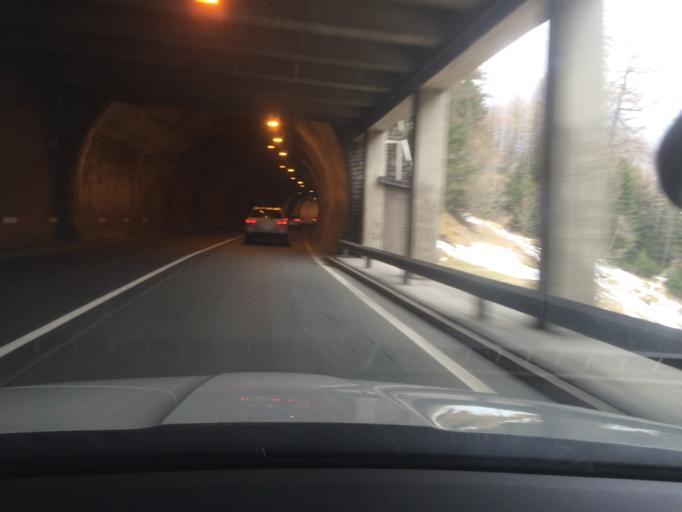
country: AT
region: Tyrol
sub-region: Politischer Bezirk Lienz
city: Matrei in Osttirol
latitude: 47.0607
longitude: 12.5270
